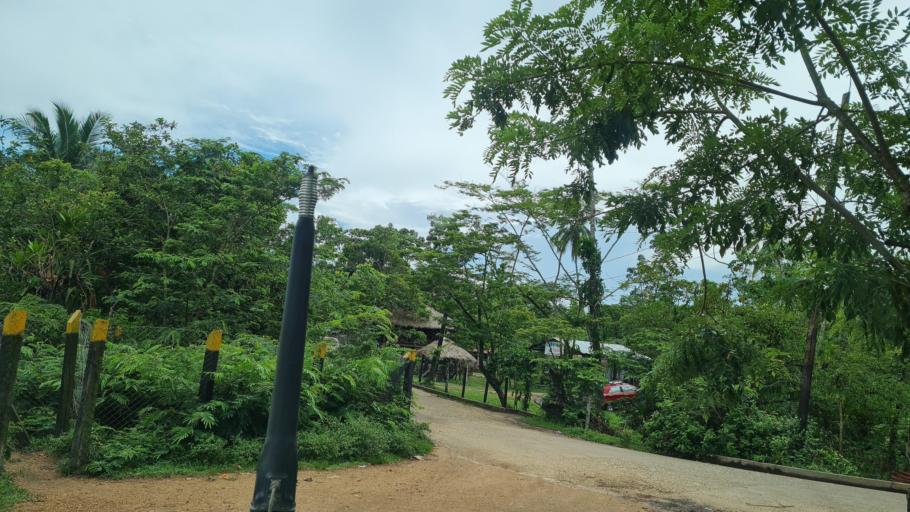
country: NI
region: Atlantico Norte (RAAN)
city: Waspam
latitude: 14.7427
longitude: -83.9675
